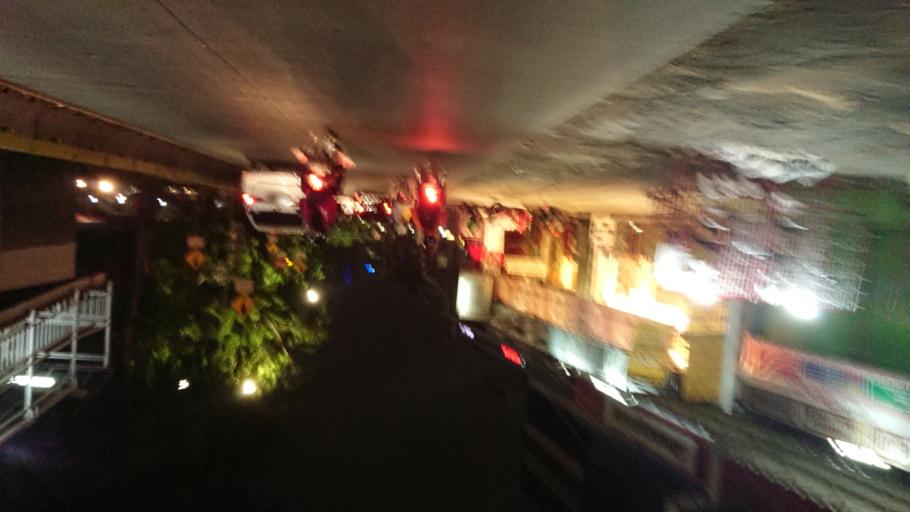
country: ID
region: Banten
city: South Tangerang
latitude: -6.2530
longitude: 106.7817
